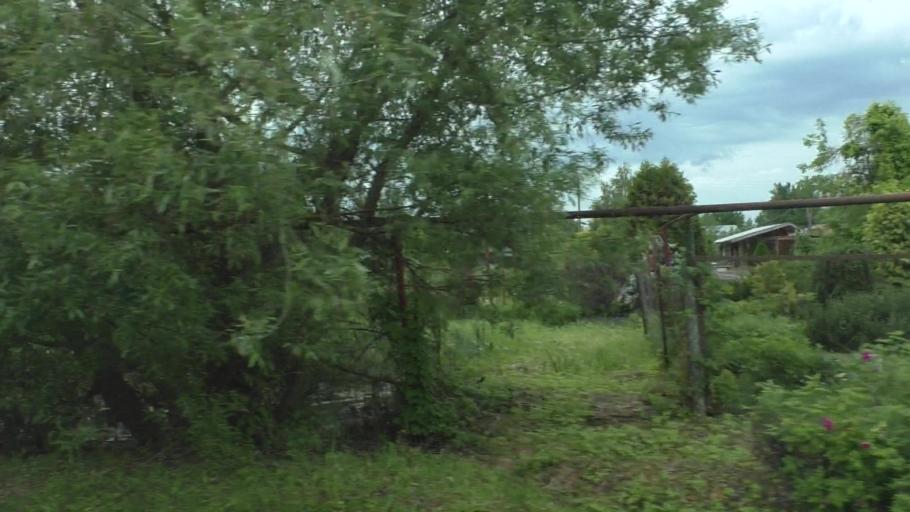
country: RU
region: Moskovskaya
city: Il'inskiy Pogost
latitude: 55.4700
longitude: 38.8965
